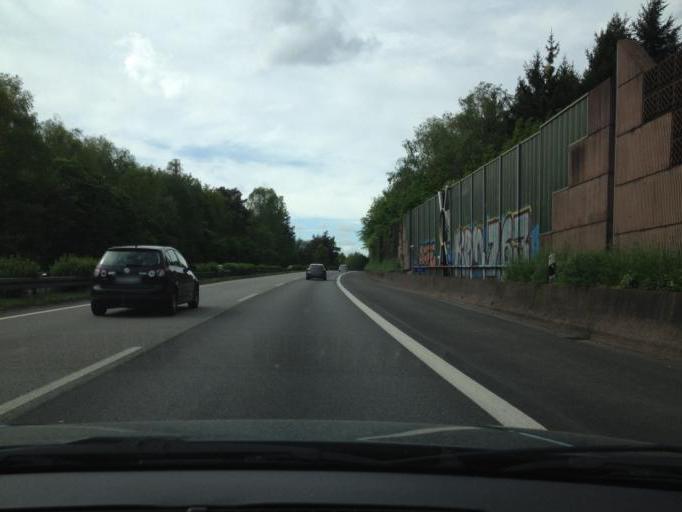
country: DE
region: Saarland
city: Kirkel
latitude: 49.3145
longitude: 7.2423
